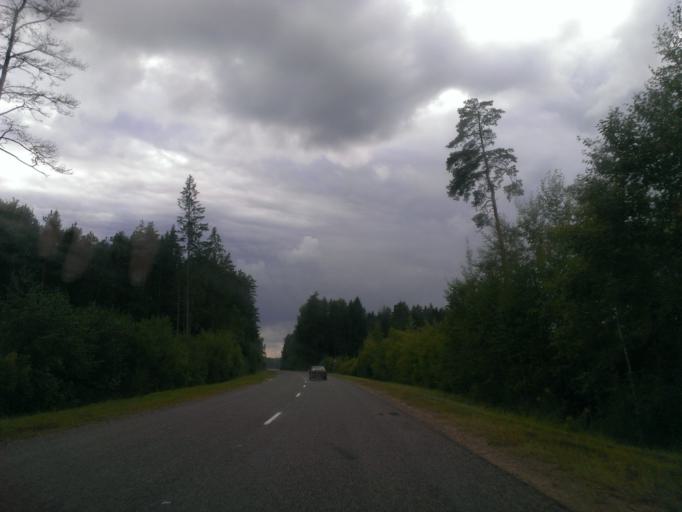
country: LV
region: Kegums
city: Kegums
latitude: 56.7656
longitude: 24.7589
